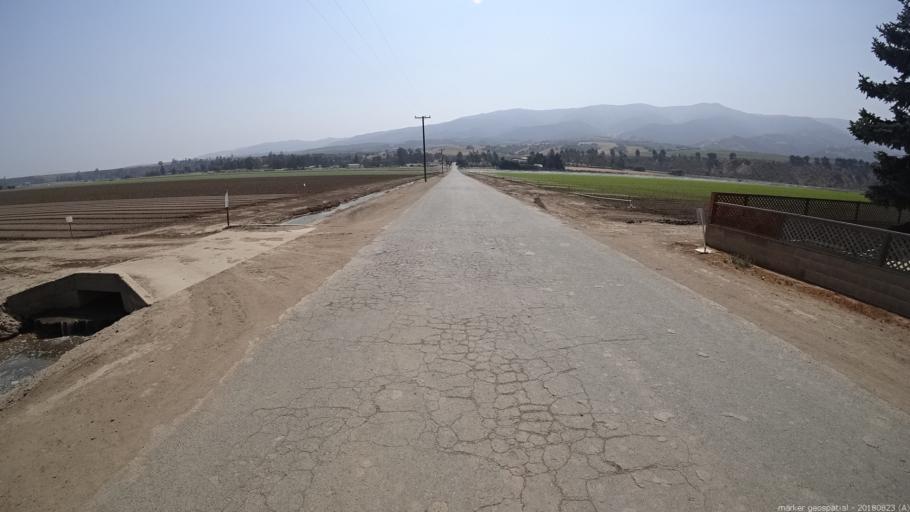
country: US
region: California
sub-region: Monterey County
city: Soledad
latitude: 36.3987
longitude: -121.3636
